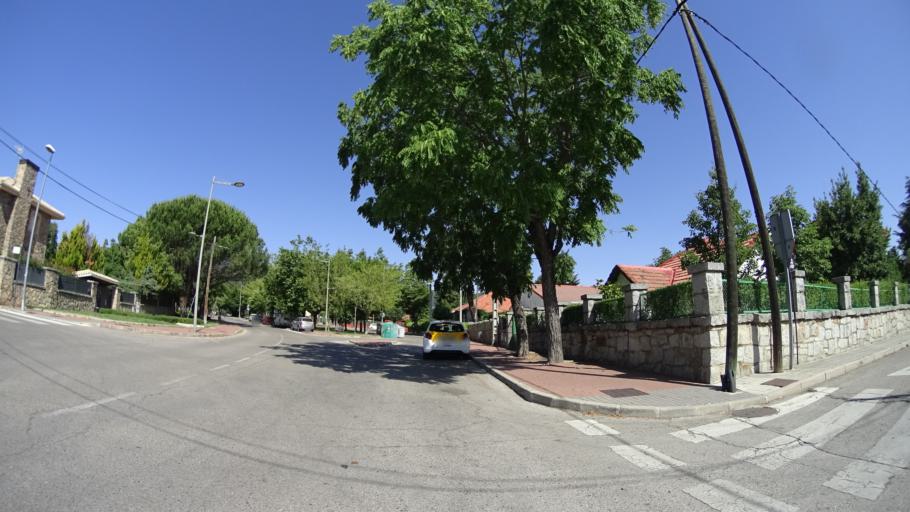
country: ES
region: Madrid
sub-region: Provincia de Madrid
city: Guadarrama
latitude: 40.6788
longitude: -4.0951
